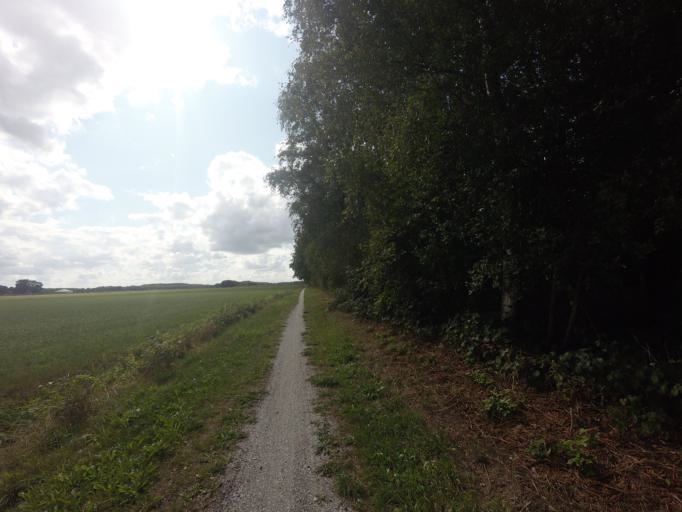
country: NL
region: Friesland
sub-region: Gemeente Weststellingwerf
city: Noordwolde
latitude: 52.9642
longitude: 6.2732
